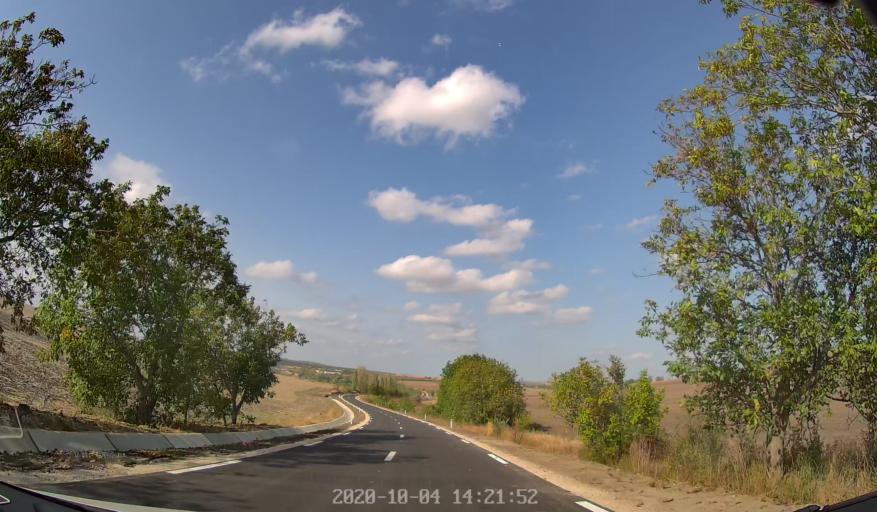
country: MD
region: Rezina
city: Saharna
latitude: 47.5904
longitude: 28.9529
